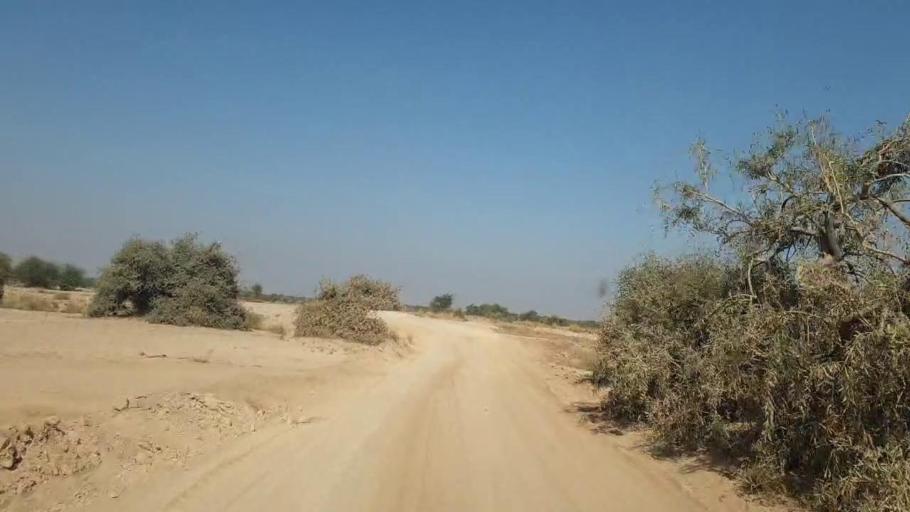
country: PK
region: Sindh
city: Jamshoro
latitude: 25.2743
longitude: 67.8071
